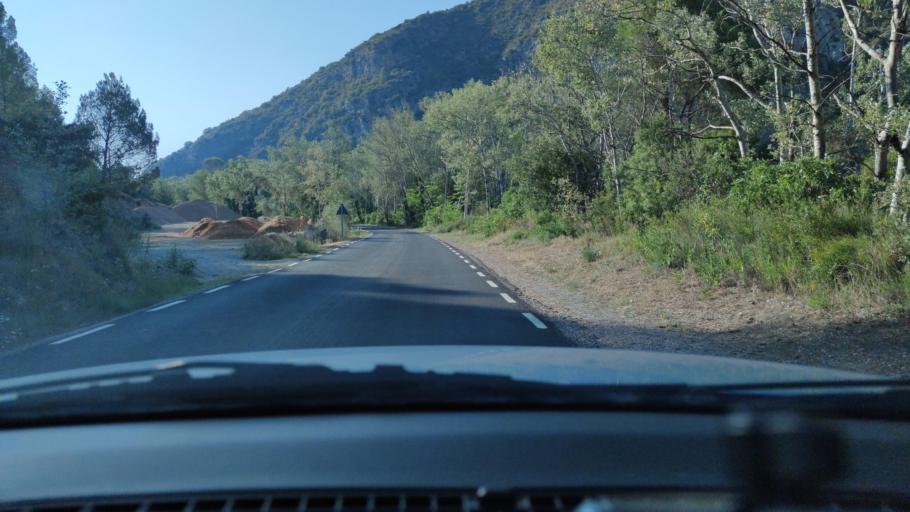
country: ES
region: Catalonia
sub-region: Provincia de Lleida
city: Camarasa
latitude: 41.8734
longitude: 0.8523
